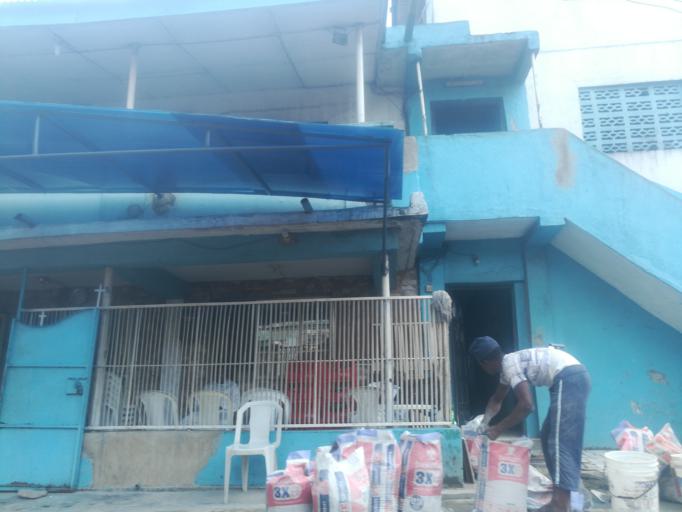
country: NG
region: Lagos
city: Somolu
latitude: 6.5516
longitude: 3.3944
